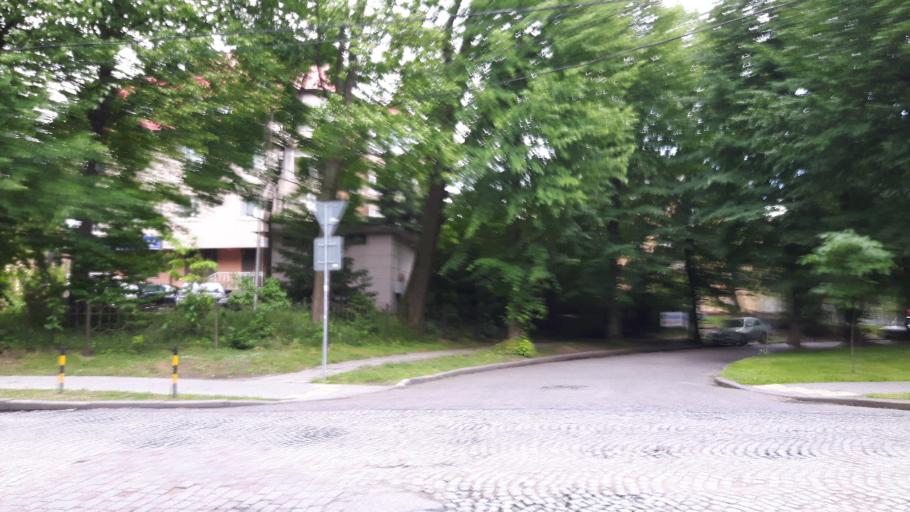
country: RU
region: Kaliningrad
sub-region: Gorod Kaliningrad
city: Kaliningrad
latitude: 54.7334
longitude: 20.5203
